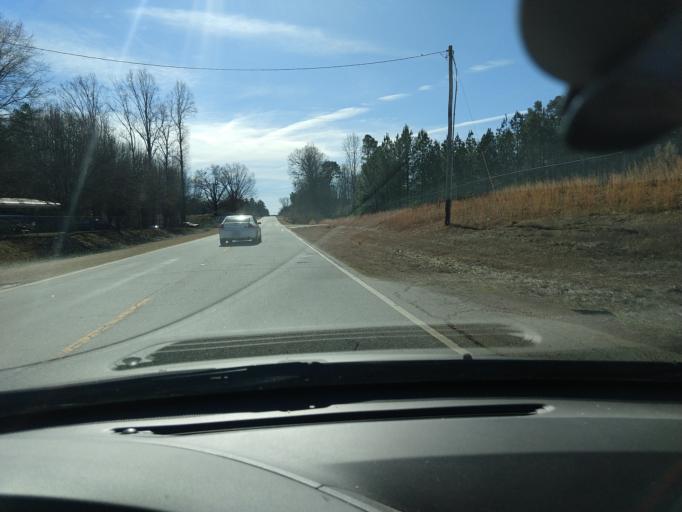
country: US
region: South Carolina
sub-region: Oconee County
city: Westminster
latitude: 34.6505
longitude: -83.1333
